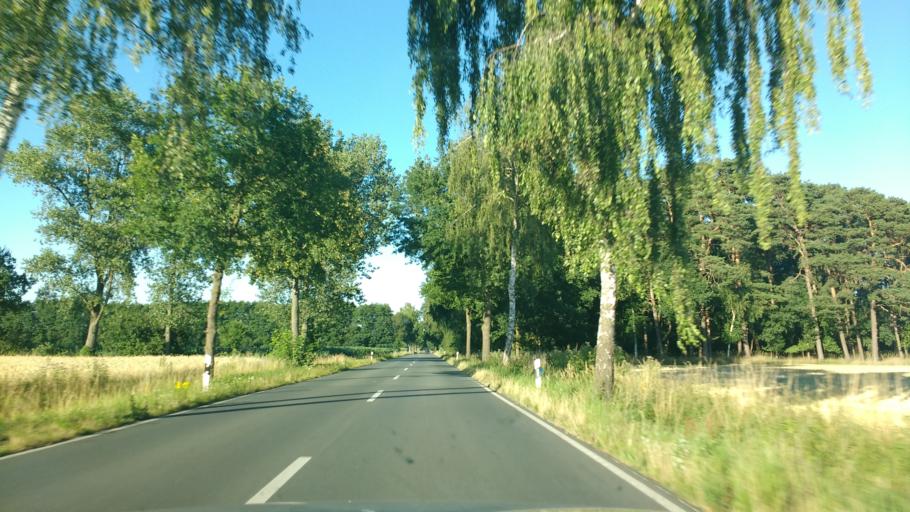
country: DE
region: North Rhine-Westphalia
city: Rietberg
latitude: 51.7210
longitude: 8.4507
